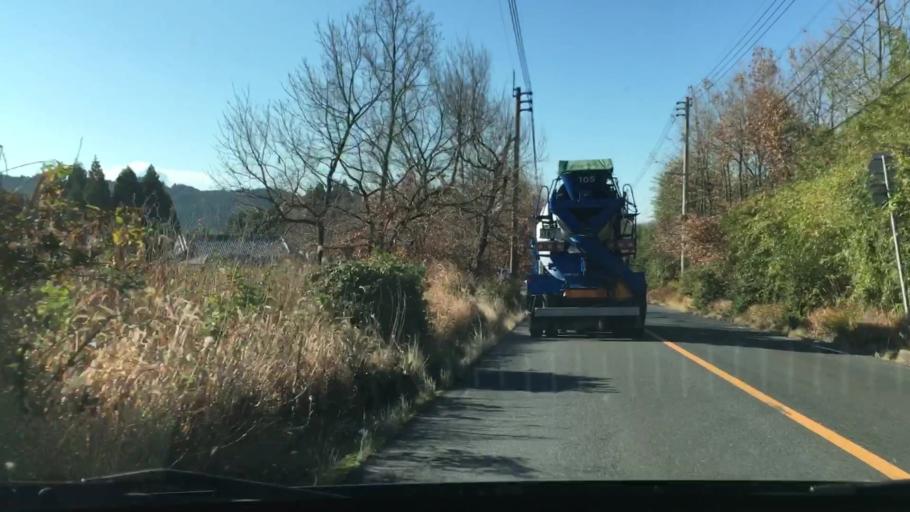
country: JP
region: Kagoshima
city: Kajiki
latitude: 31.7668
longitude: 130.6908
